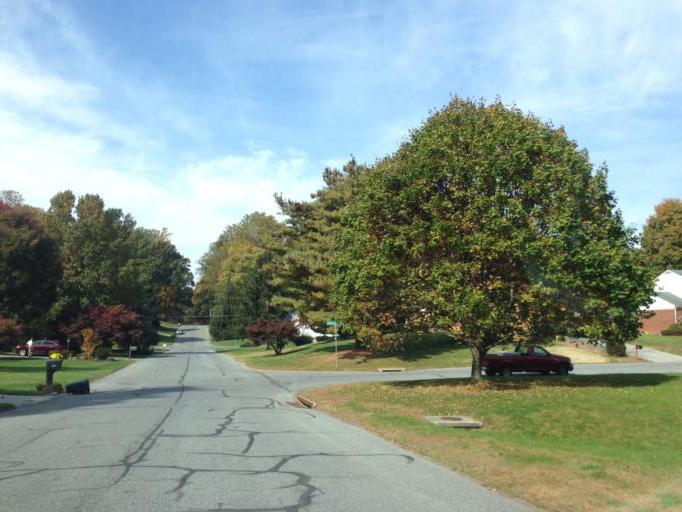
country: US
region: Maryland
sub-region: Howard County
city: Columbia
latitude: 39.2858
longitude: -76.8509
